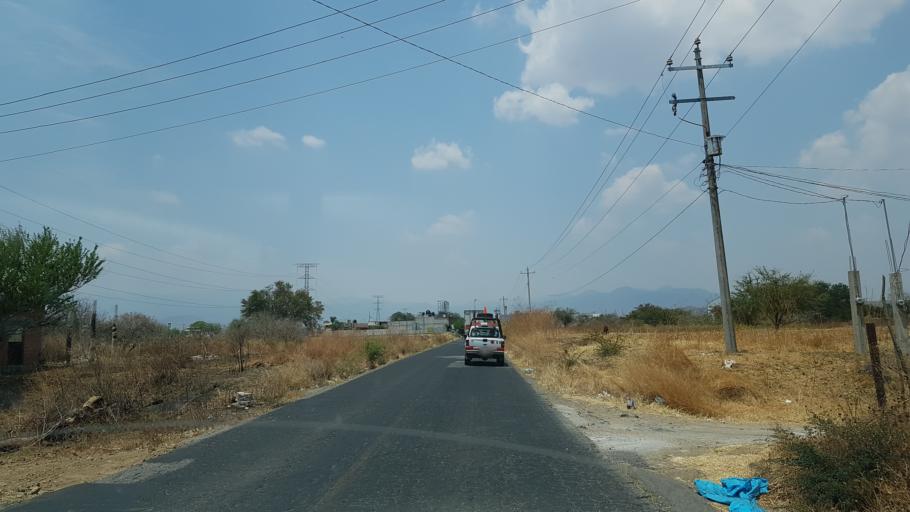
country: MX
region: Morelos
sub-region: Yecapixtla
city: Yecapixtla
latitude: 18.8871
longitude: -98.8849
